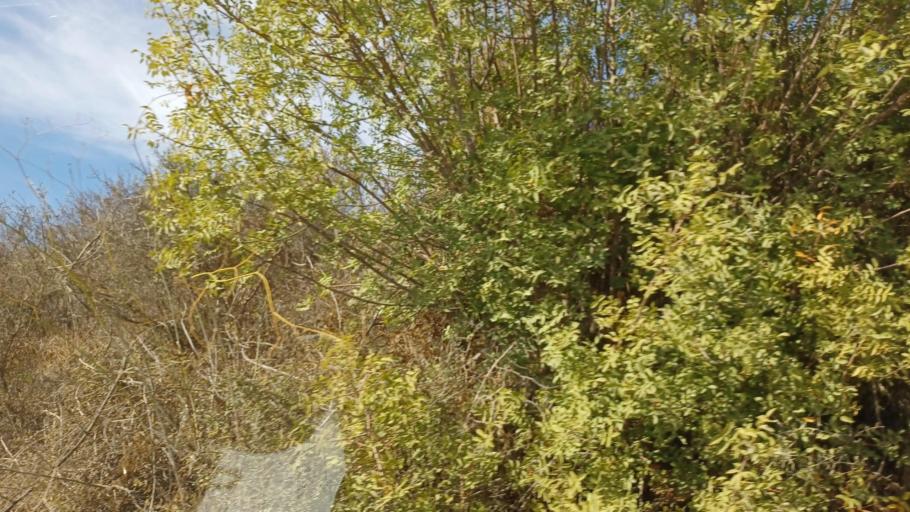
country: CY
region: Pafos
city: Pegeia
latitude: 34.9326
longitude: 32.4516
